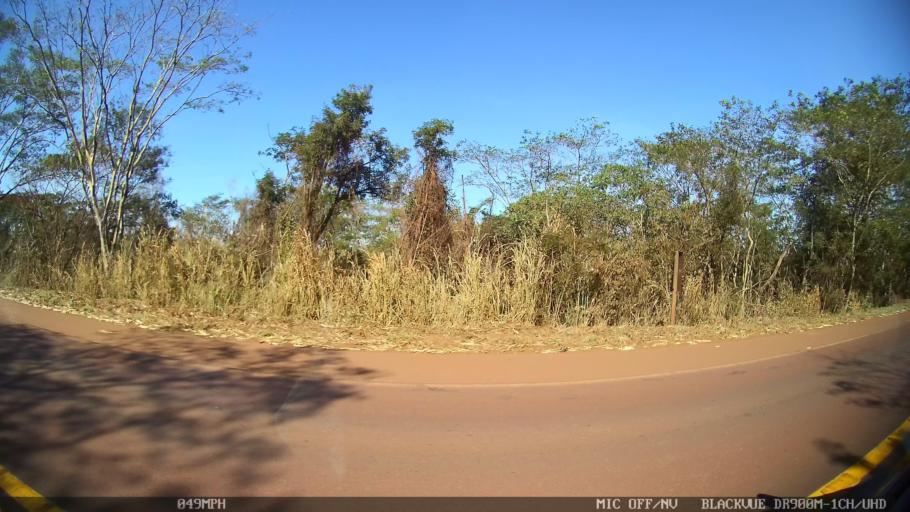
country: BR
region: Sao Paulo
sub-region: Barretos
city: Barretos
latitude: -20.4548
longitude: -48.4591
